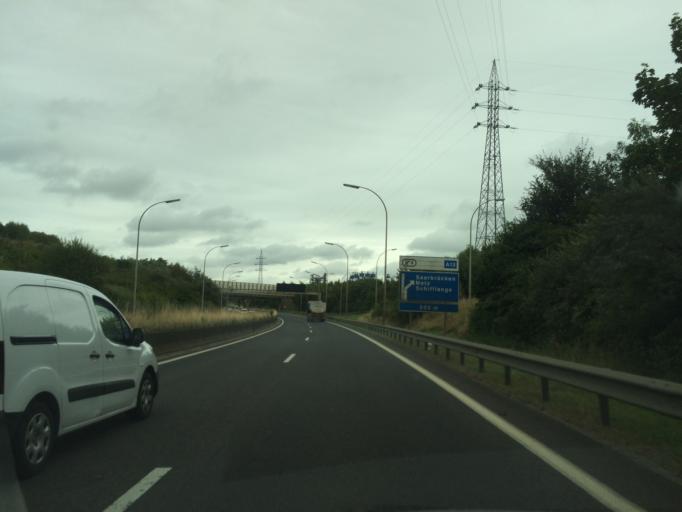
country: LU
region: Luxembourg
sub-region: Canton d'Esch-sur-Alzette
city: Mondercange
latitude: 49.5150
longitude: 5.9928
